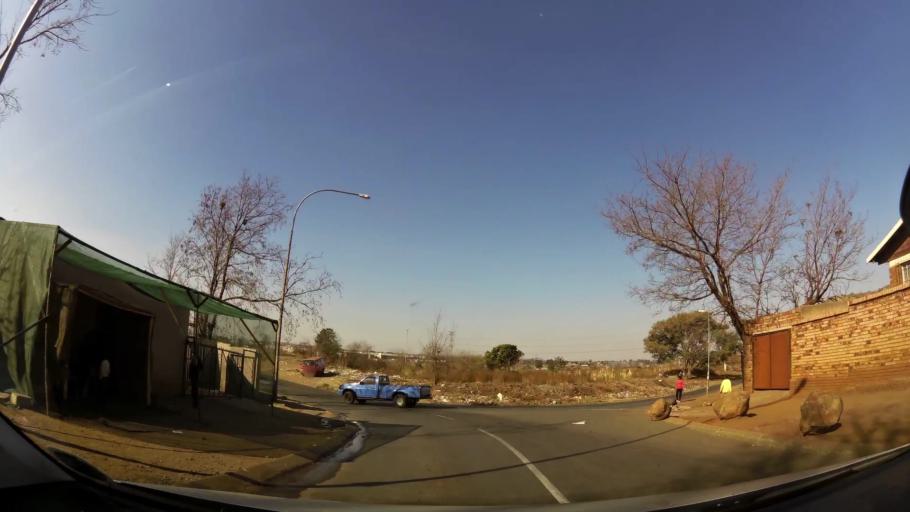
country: ZA
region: Gauteng
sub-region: City of Johannesburg Metropolitan Municipality
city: Soweto
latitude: -26.2801
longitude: 27.8754
